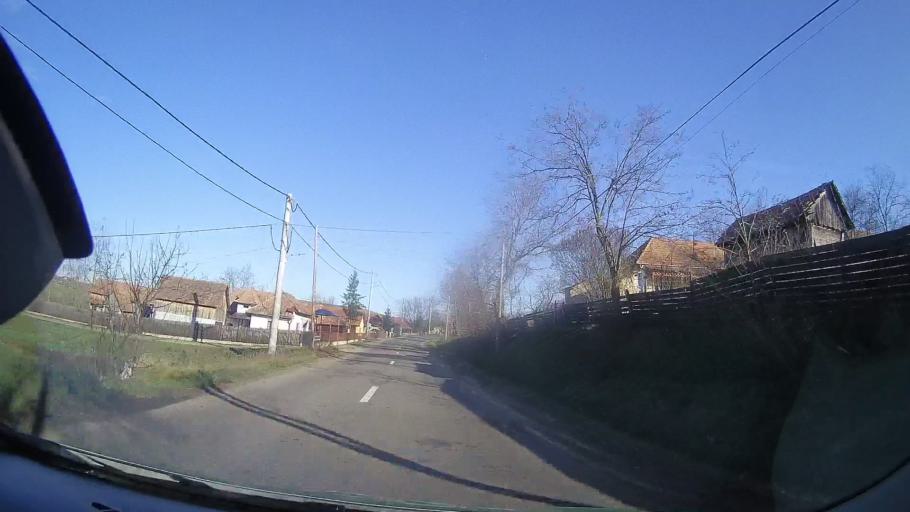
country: RO
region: Mures
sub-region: Comuna Band
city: Band
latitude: 46.5786
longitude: 24.3527
